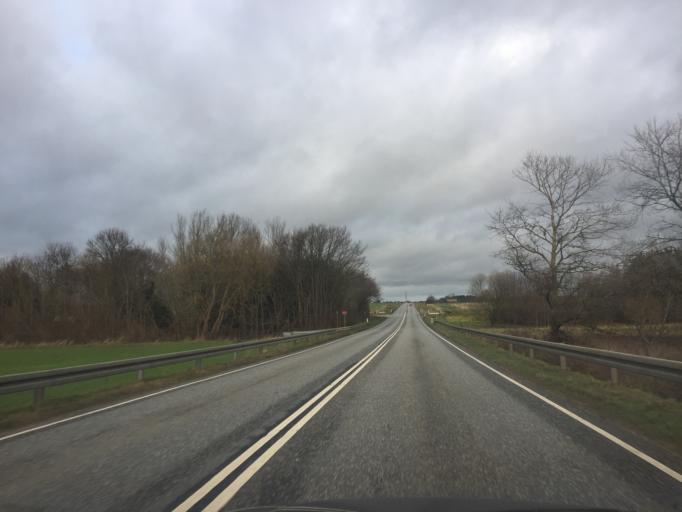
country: DK
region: Zealand
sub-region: Soro Kommune
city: Soro
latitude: 55.4767
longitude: 11.5676
